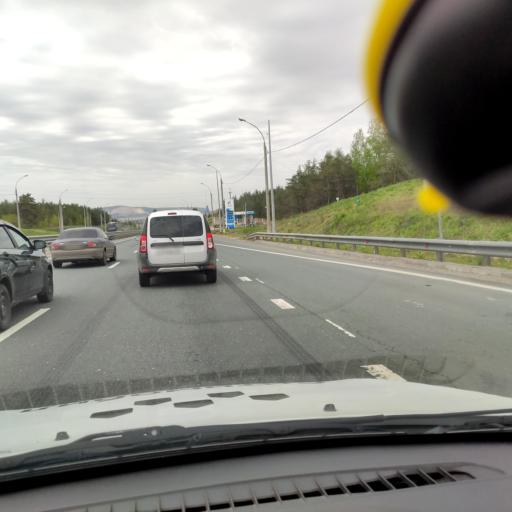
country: RU
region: Samara
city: Zhigulevsk
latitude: 53.4969
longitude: 49.5348
